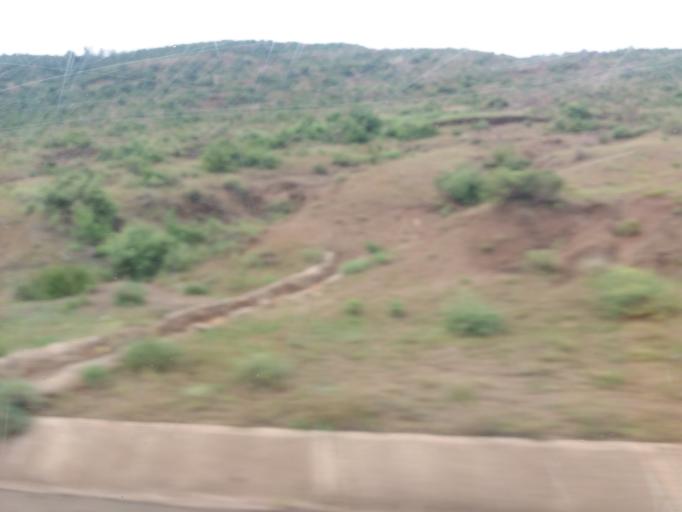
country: LS
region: Berea
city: Teyateyaneng
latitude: -29.3242
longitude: 27.7589
